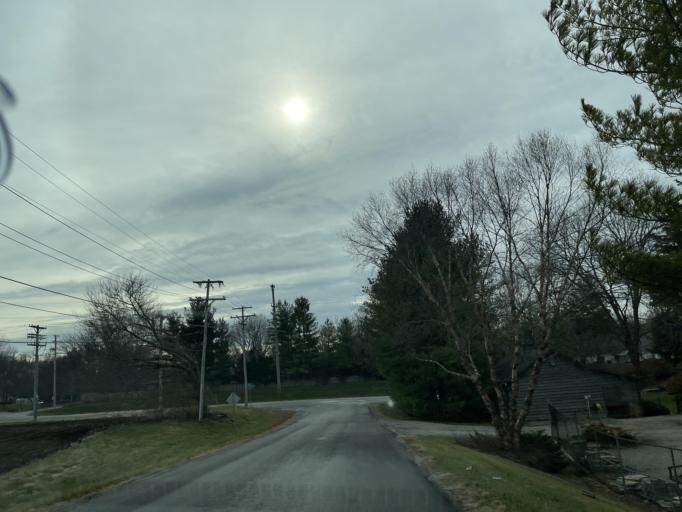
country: US
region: Illinois
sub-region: Sangamon County
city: Leland Grove
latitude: 39.7874
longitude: -89.7296
